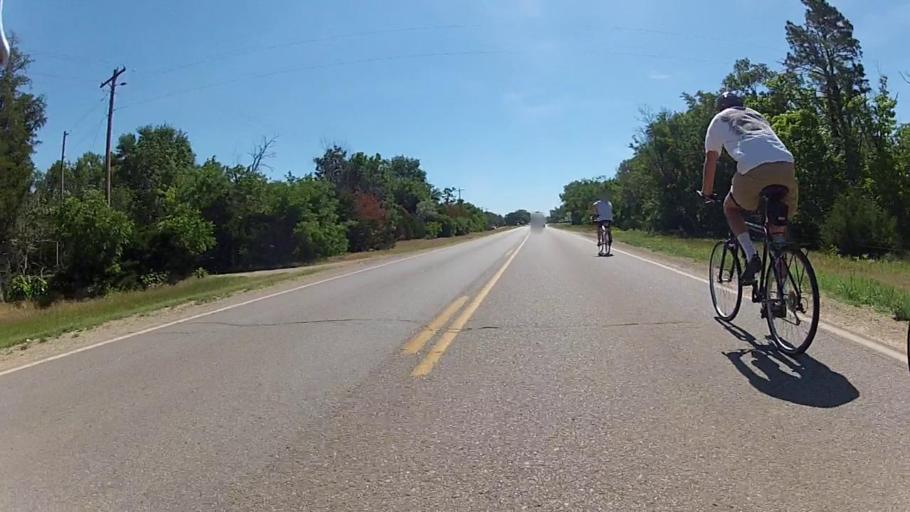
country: US
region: Kansas
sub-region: Barber County
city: Medicine Lodge
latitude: 37.2753
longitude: -98.6017
